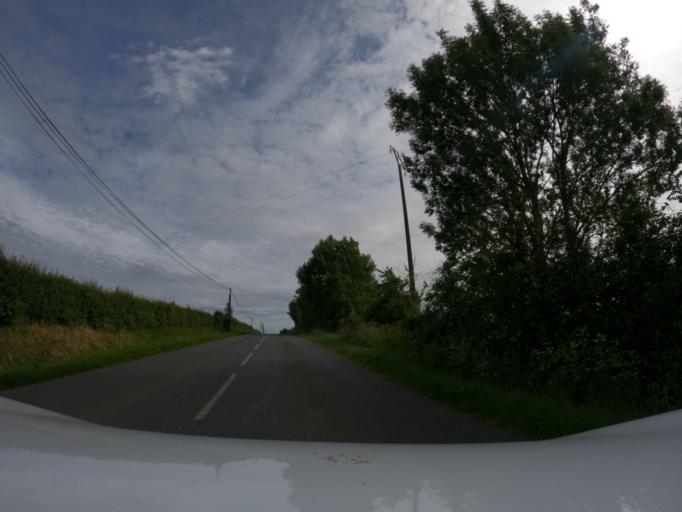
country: FR
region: Pays de la Loire
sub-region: Departement de la Vendee
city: Saint-Hilaire-des-Loges
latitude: 46.4866
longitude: -0.6629
